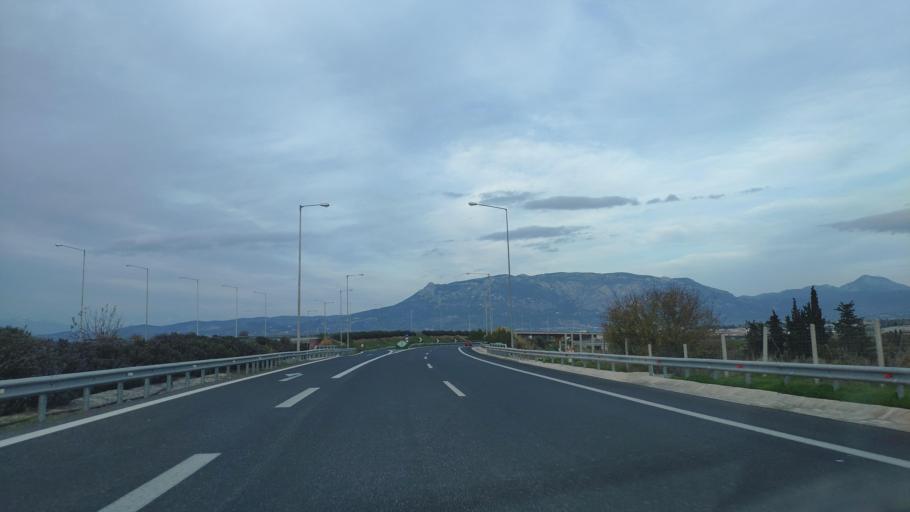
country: GR
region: Peloponnese
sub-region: Nomos Korinthias
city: Arkhaia Korinthos
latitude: 37.9153
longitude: 22.9077
